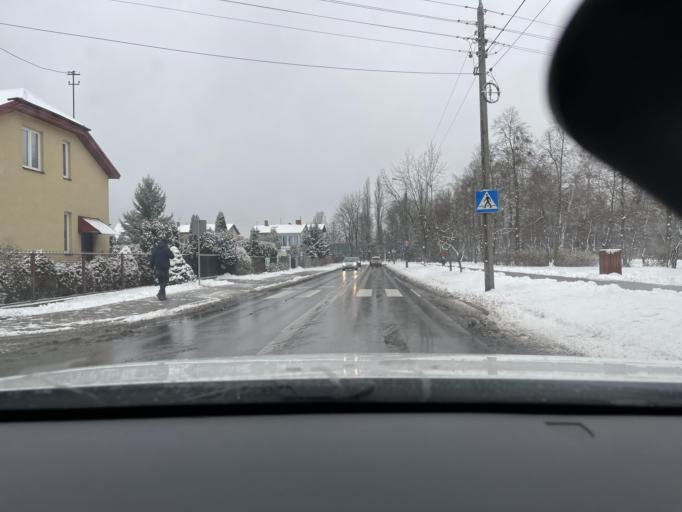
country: PL
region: Masovian Voivodeship
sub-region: Powiat zyrardowski
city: Zyrardow
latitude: 52.0474
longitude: 20.4396
